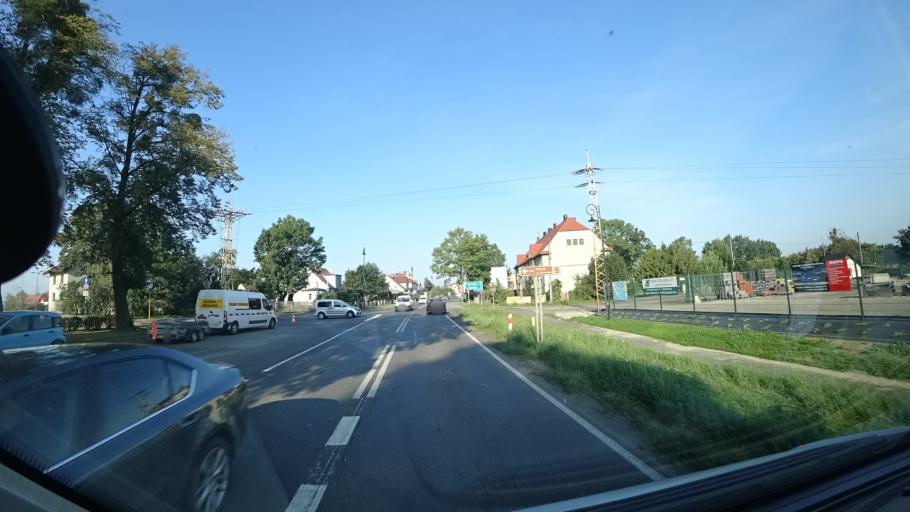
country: PL
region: Silesian Voivodeship
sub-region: Powiat gliwicki
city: Sosnicowice
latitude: 50.2705
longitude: 18.5359
